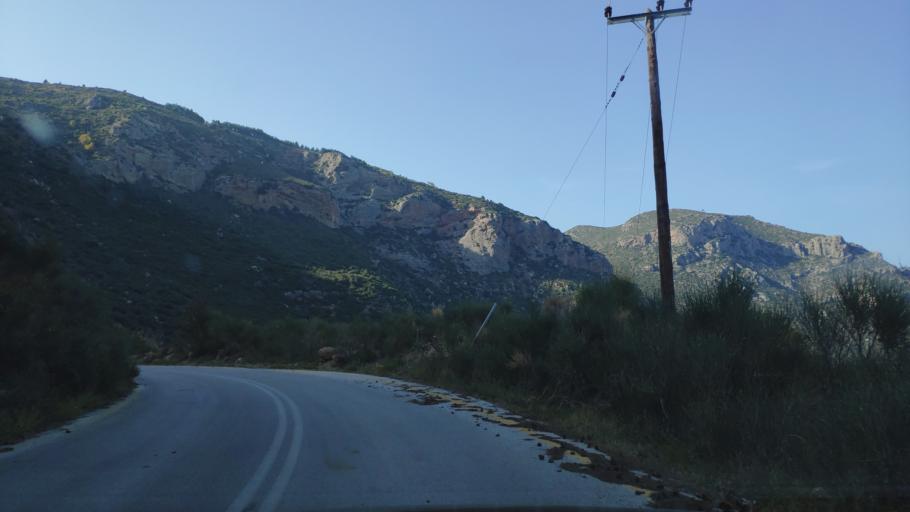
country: GR
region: West Greece
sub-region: Nomos Achaias
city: Aiyira
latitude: 38.0591
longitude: 22.3808
